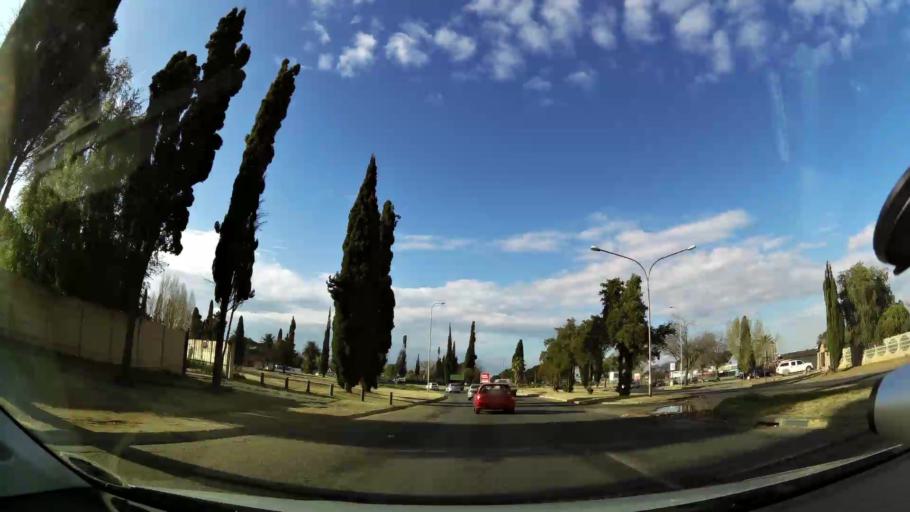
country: ZA
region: Orange Free State
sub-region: Lejweleputswa District Municipality
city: Welkom
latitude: -27.9878
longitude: 26.7548
